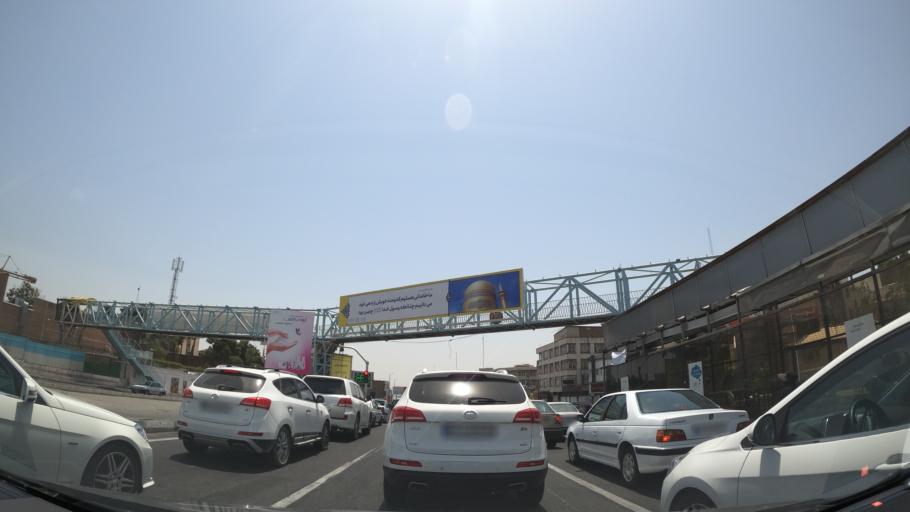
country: IR
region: Tehran
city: Tehran
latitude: 35.7066
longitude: 51.3776
